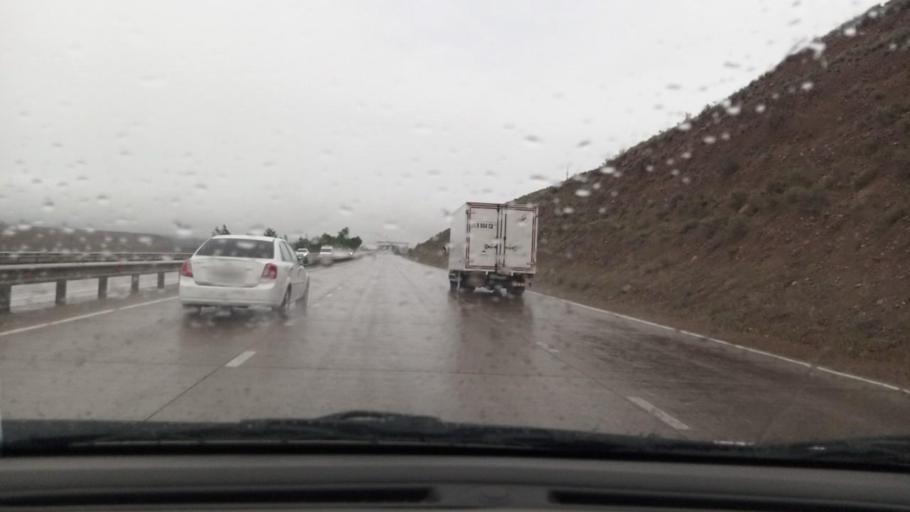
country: UZ
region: Namangan
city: Pop Shahri
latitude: 40.9248
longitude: 70.7263
